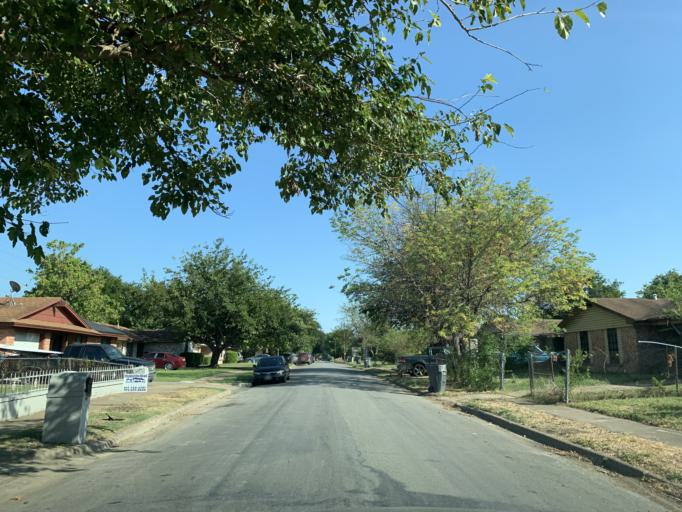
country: US
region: Texas
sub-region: Dallas County
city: Hutchins
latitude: 32.6609
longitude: -96.7690
